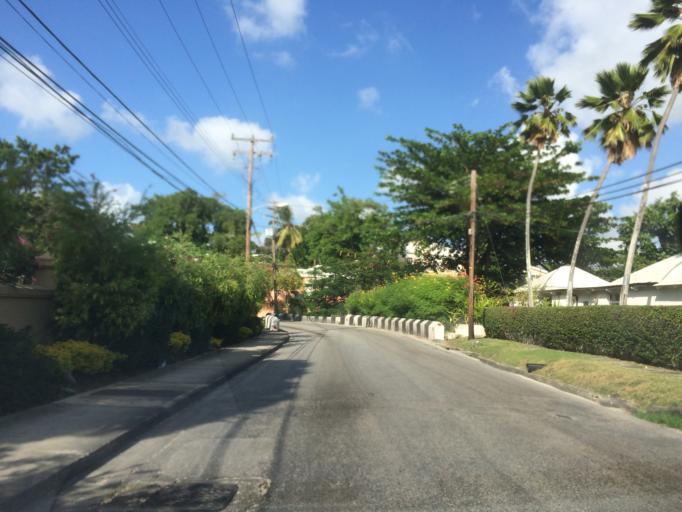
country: BB
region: Saint James
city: Holetown
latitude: 13.1566
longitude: -59.6365
